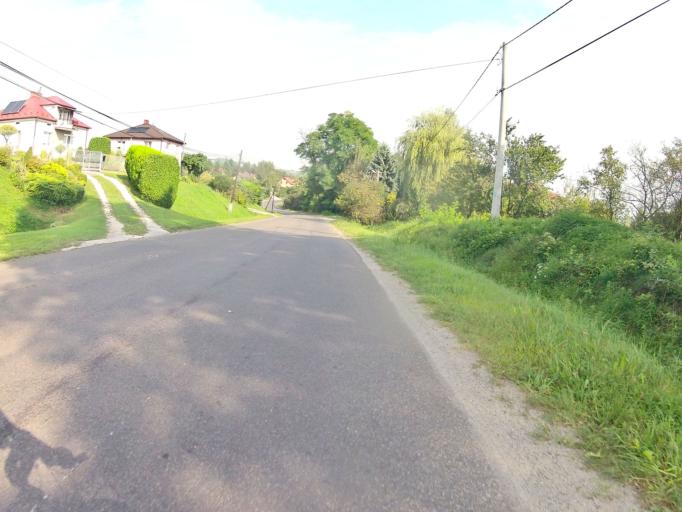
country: PL
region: Subcarpathian Voivodeship
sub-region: Powiat jasielski
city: Trzcinica
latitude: 49.7780
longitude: 21.4058
